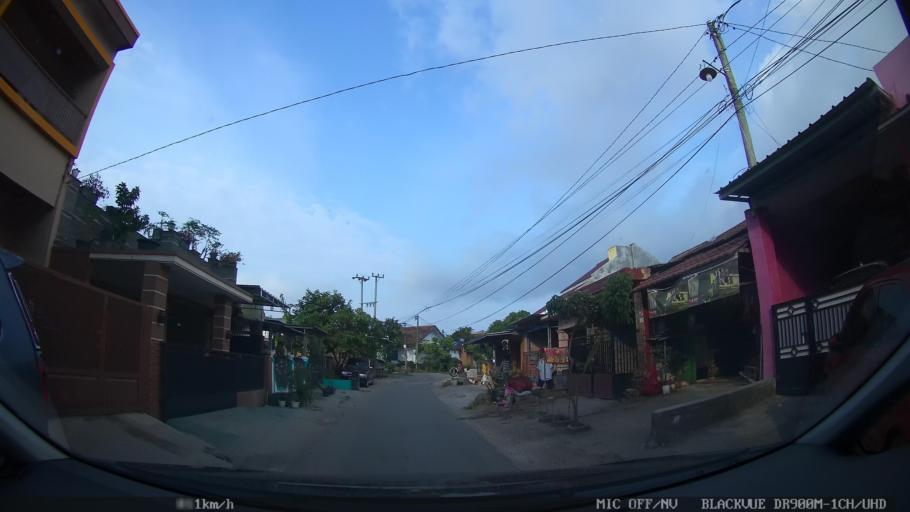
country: ID
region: Lampung
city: Kedaton
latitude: -5.4031
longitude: 105.3072
